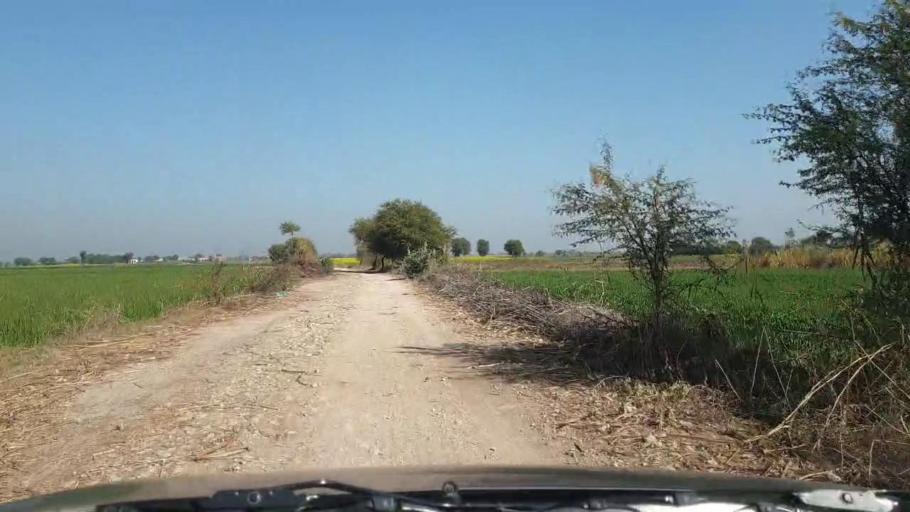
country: PK
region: Sindh
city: Jhol
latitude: 25.9584
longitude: 68.8223
